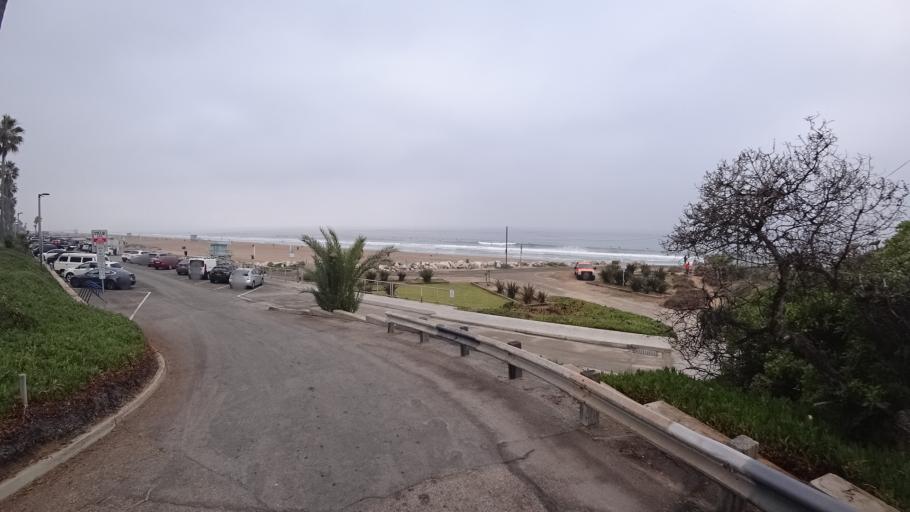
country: US
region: California
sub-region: Los Angeles County
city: El Segundo
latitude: 33.9053
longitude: -118.4221
